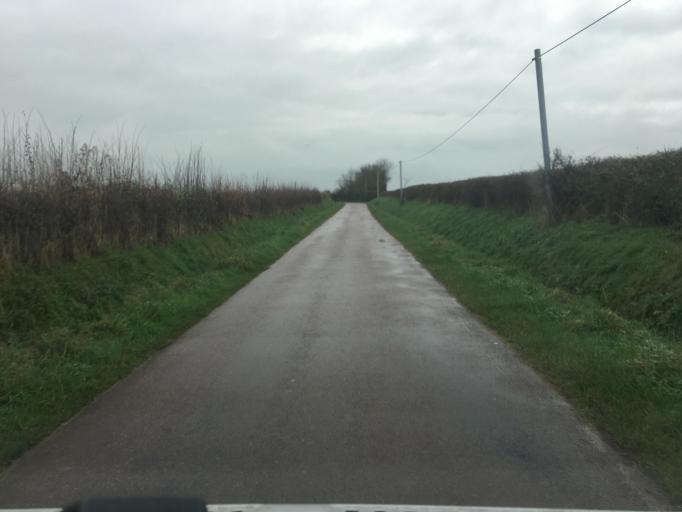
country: FR
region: Lower Normandy
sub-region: Departement de la Manche
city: Sainte-Mere-Eglise
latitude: 49.4340
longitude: -1.2611
